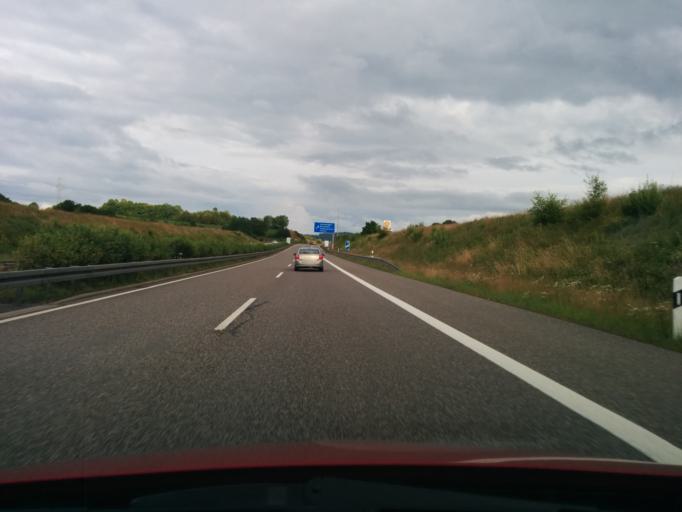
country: DE
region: Thuringia
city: Sankt Kilian
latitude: 50.5197
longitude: 10.7608
